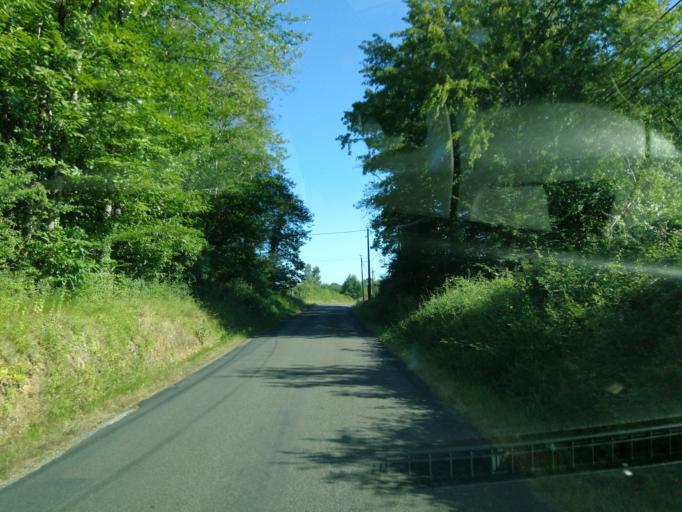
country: FR
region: Midi-Pyrenees
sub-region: Departement du Lot
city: Gourdon
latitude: 44.7720
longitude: 1.3680
